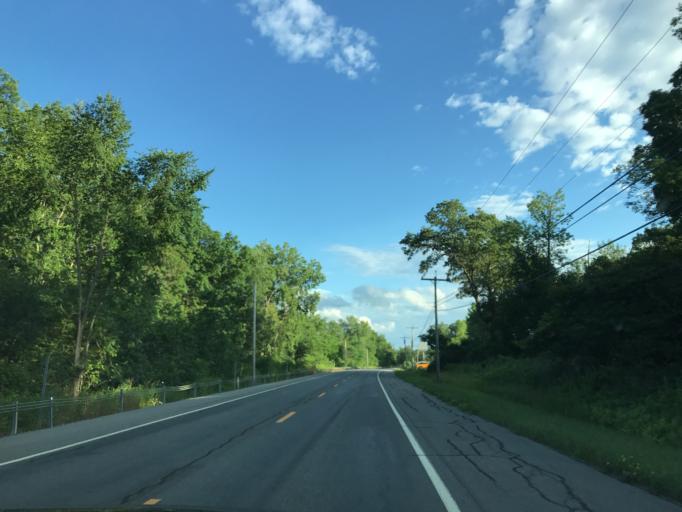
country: US
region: New York
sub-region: Saratoga County
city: Schuylerville
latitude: 43.1354
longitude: -73.5847
